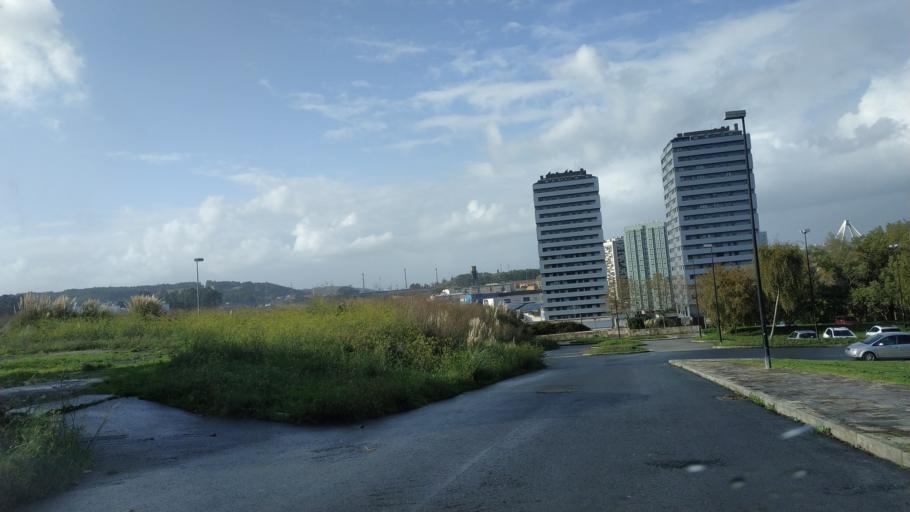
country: ES
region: Galicia
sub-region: Provincia da Coruna
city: A Coruna
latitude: 43.3334
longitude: -8.4066
